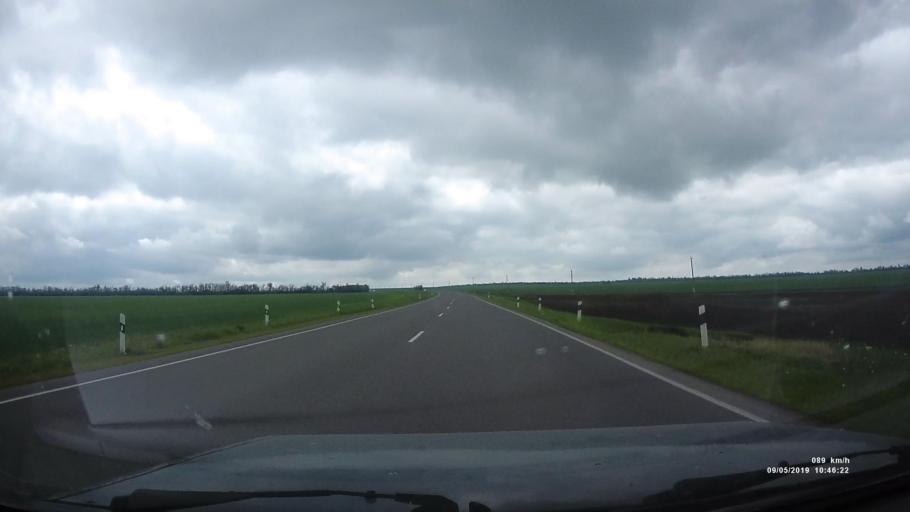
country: RU
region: Rostov
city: Peshkovo
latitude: 46.9855
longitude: 39.3568
